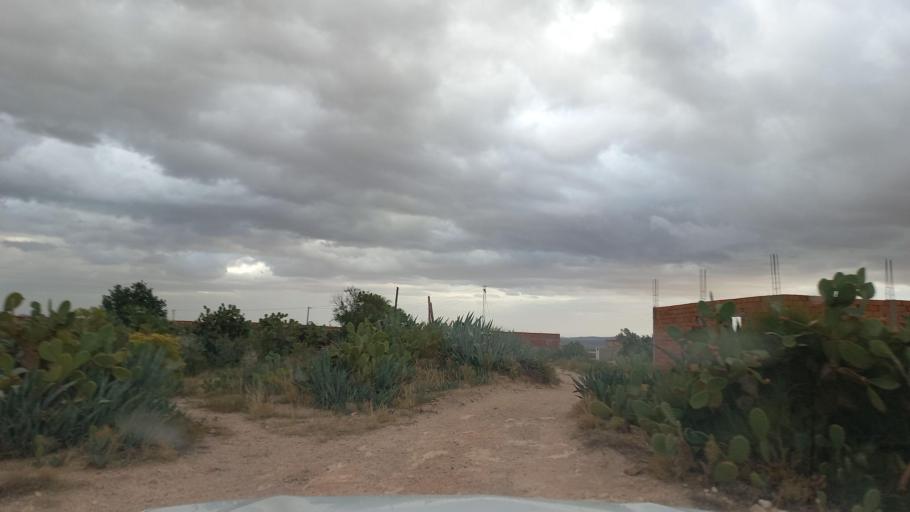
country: TN
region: Al Qasrayn
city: Kasserine
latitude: 35.2743
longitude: 8.9369
